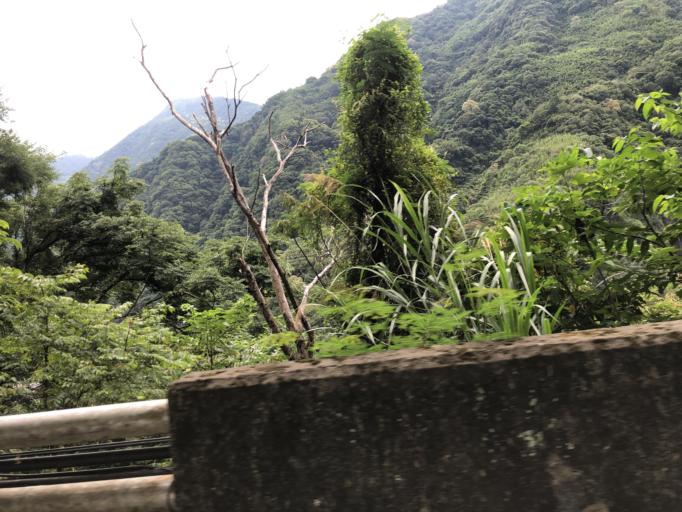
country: TW
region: Taiwan
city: Daxi
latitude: 24.6851
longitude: 121.3796
